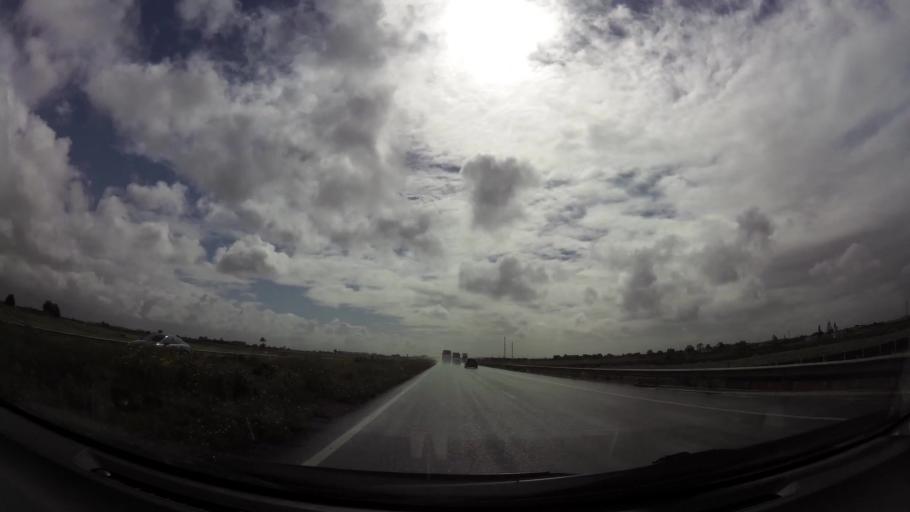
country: MA
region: Grand Casablanca
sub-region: Nouaceur
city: Dar Bouazza
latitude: 33.3576
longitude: -7.9501
